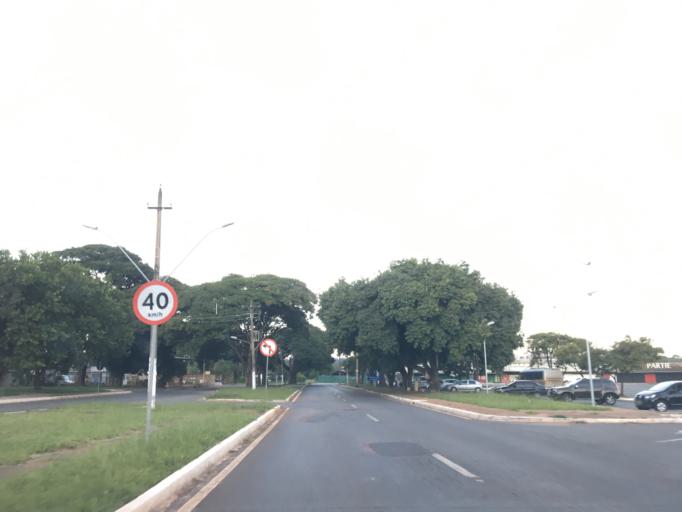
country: BR
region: Federal District
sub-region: Brasilia
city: Brasilia
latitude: -15.8253
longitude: -47.9732
